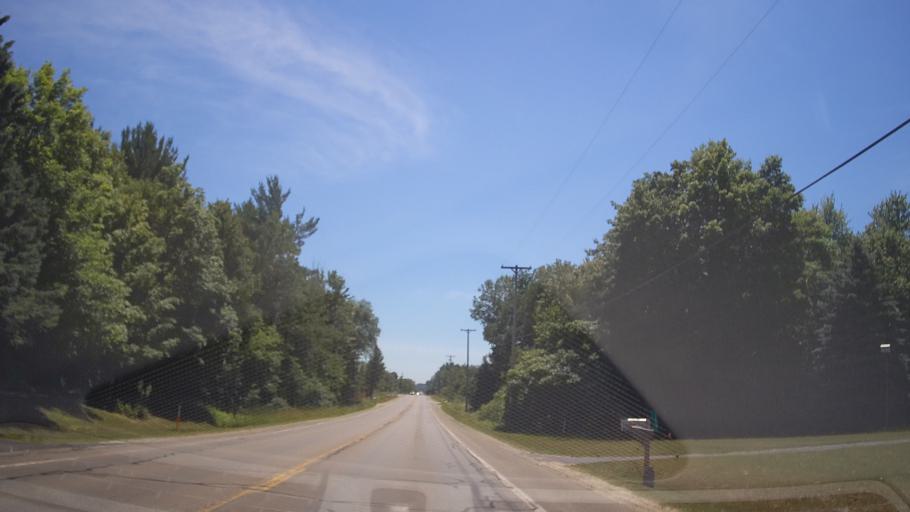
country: US
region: Michigan
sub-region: Grand Traverse County
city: Traverse City
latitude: 44.6849
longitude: -85.6895
